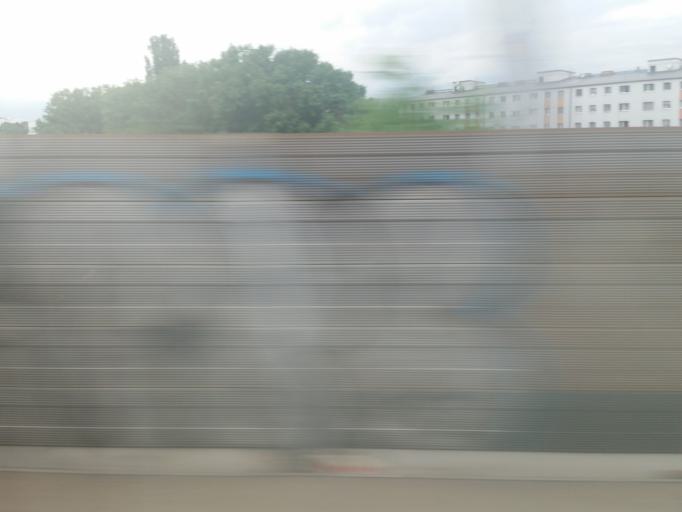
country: AT
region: Lower Austria
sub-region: Politischer Bezirk Wien-Umgebung
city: Schwechat
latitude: 48.1774
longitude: 16.4254
